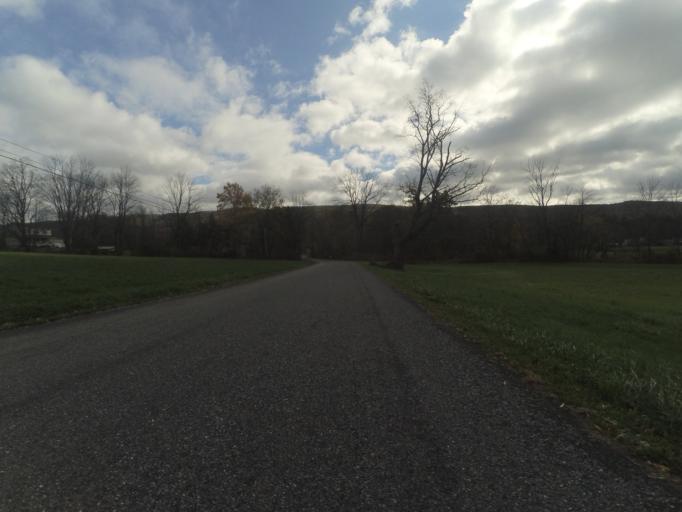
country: US
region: Pennsylvania
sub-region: Centre County
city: Park Forest Village
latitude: 40.8979
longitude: -77.8965
